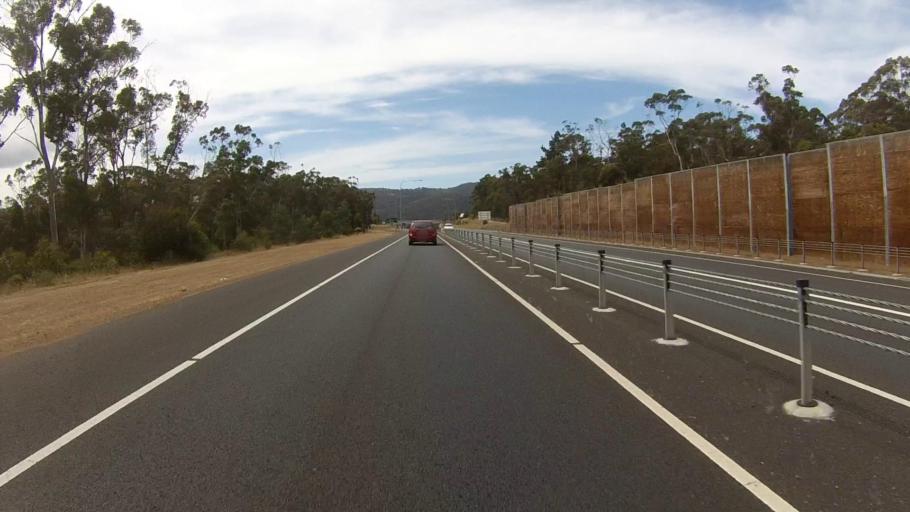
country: AU
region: Tasmania
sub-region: Kingborough
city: Kingston
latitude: -42.9785
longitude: 147.2968
